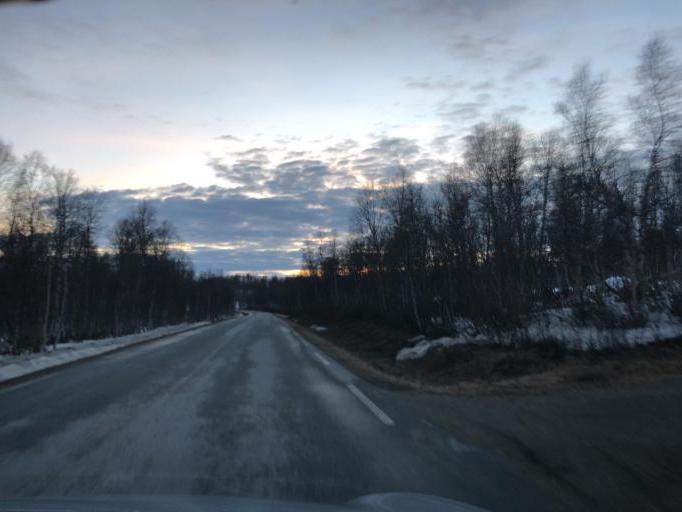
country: NO
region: Sor-Trondelag
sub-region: Tydal
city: Aas
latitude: 62.6745
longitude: 11.8058
